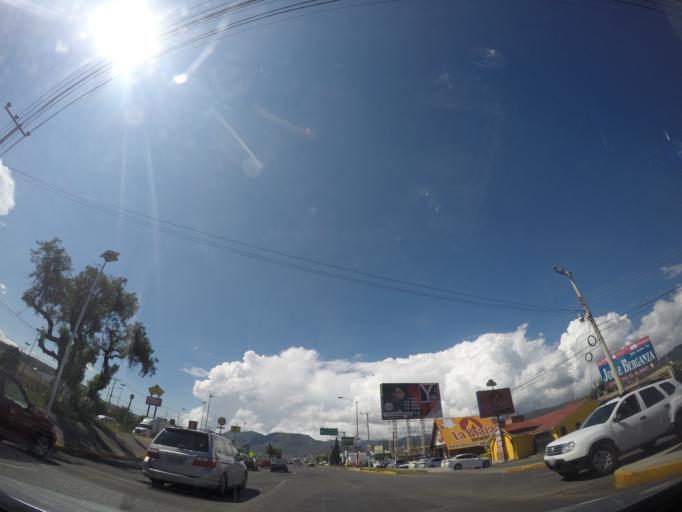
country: MX
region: Hidalgo
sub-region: Mineral de la Reforma
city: Campestre Villas del Alamo
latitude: 20.0971
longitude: -98.7155
